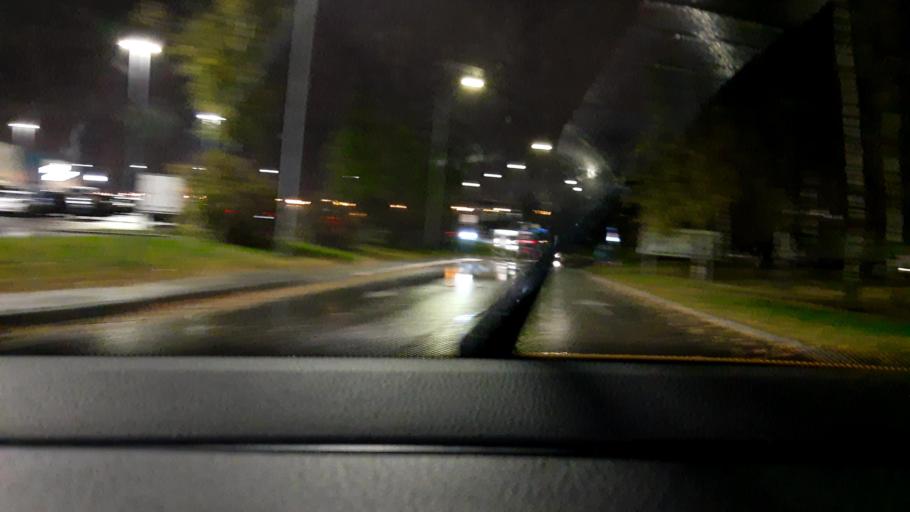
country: RU
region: Moscow
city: Lianozovo
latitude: 55.9134
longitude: 37.5753
